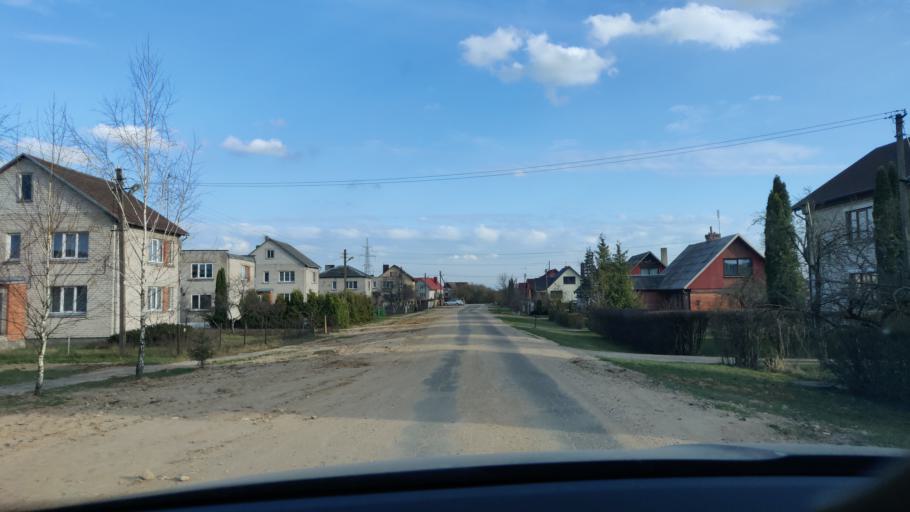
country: LT
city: Trakai
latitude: 54.6076
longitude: 24.9759
